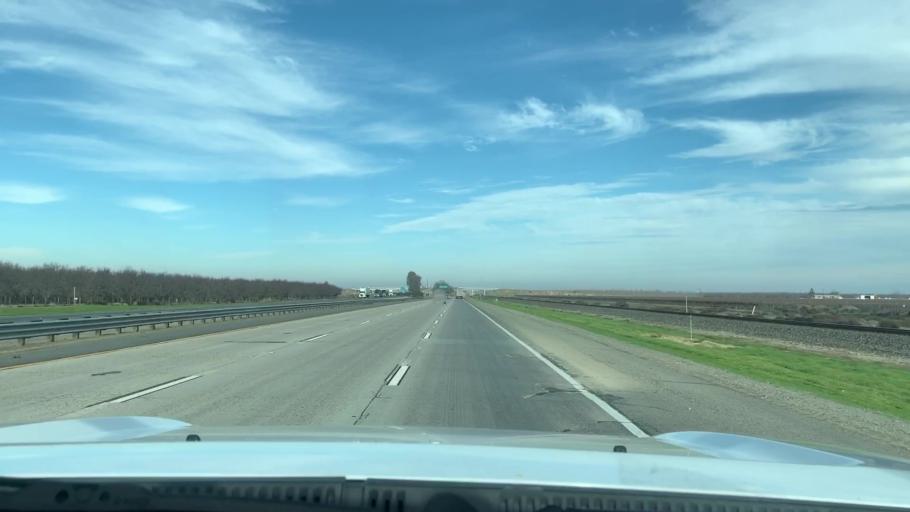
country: US
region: California
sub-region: Kern County
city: McFarland
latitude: 35.6373
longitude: -119.2175
